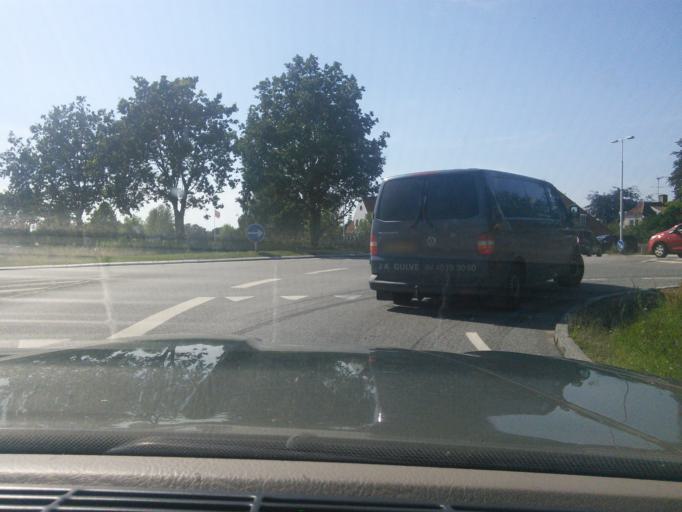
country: DK
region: Capital Region
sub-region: Halsnaes Kommune
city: Frederiksvaerk
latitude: 55.9819
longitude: 12.0211
